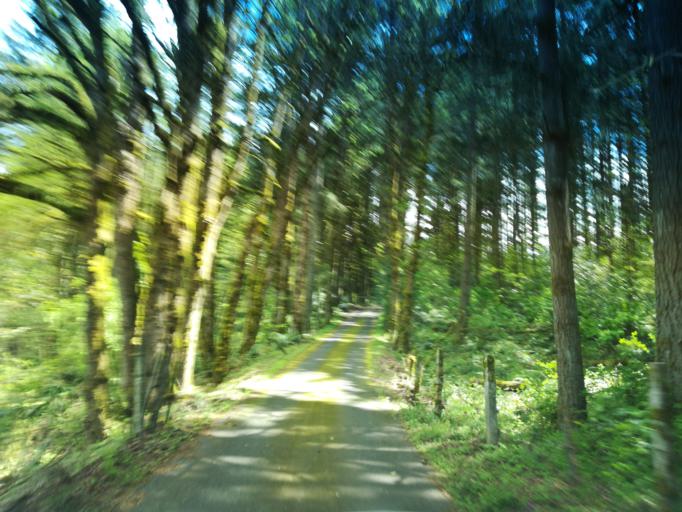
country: US
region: Oregon
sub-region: Clackamas County
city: Damascus
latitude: 45.4279
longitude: -122.4541
